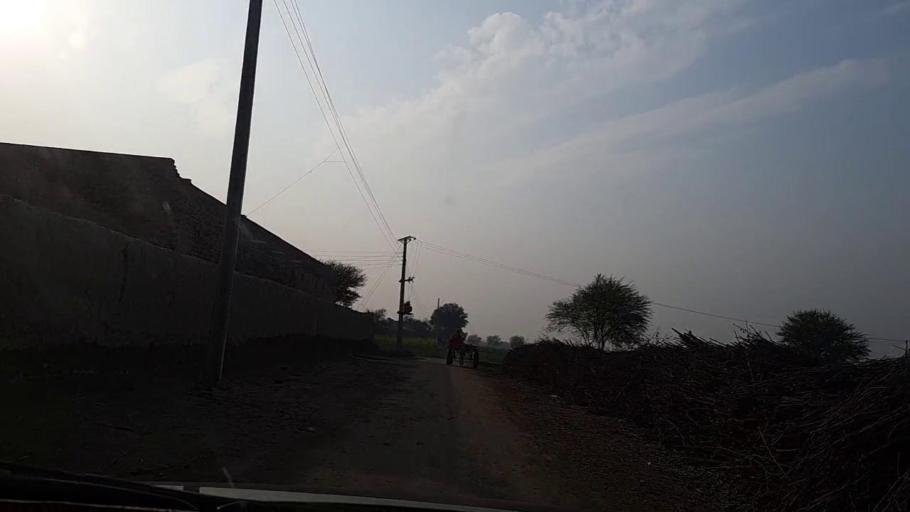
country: PK
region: Sindh
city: Nawabshah
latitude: 26.2673
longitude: 68.3111
